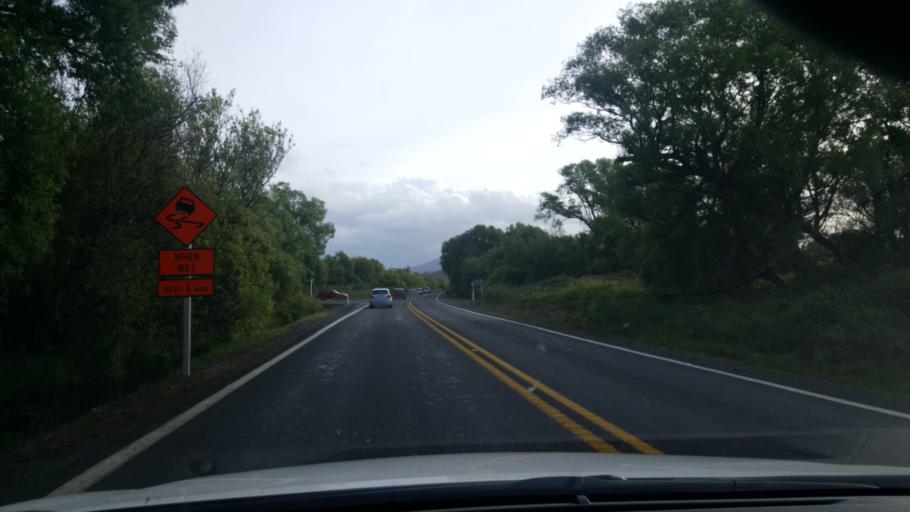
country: NZ
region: Waikato
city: Turangi
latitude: -38.9479
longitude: 175.8502
